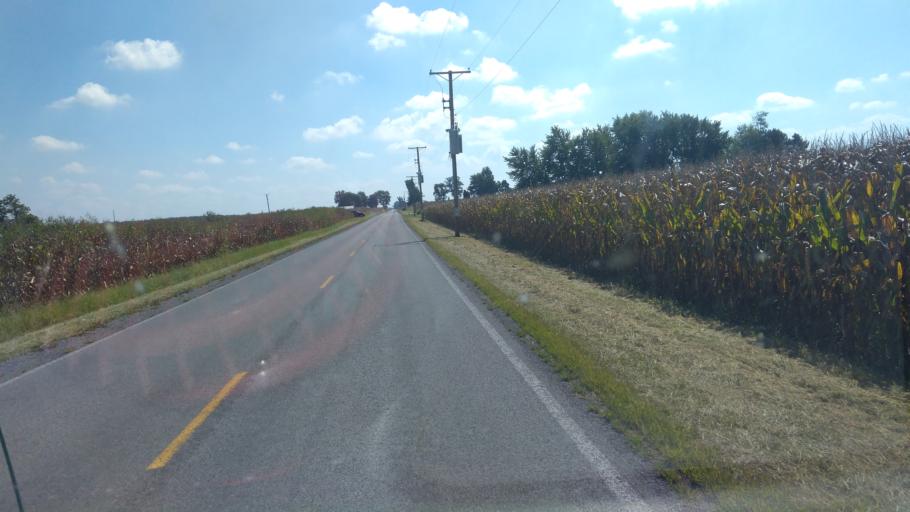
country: US
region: Ohio
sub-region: Hardin County
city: Ada
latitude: 40.7711
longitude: -83.7849
